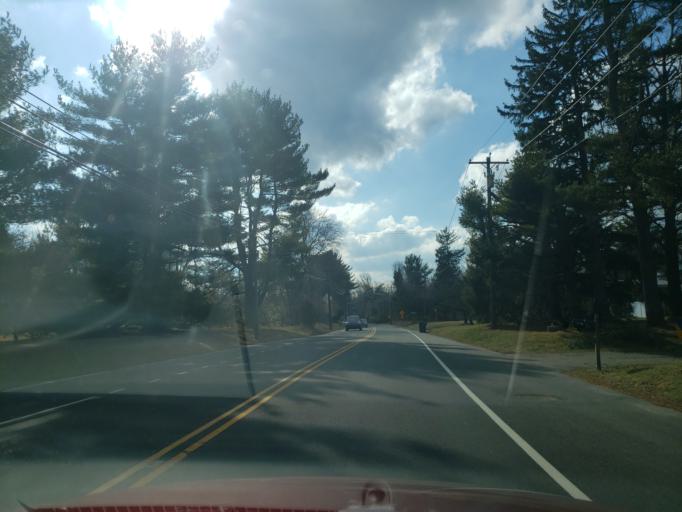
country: US
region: New Jersey
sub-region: Hunterdon County
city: Flemington
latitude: 40.5010
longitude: -74.8741
